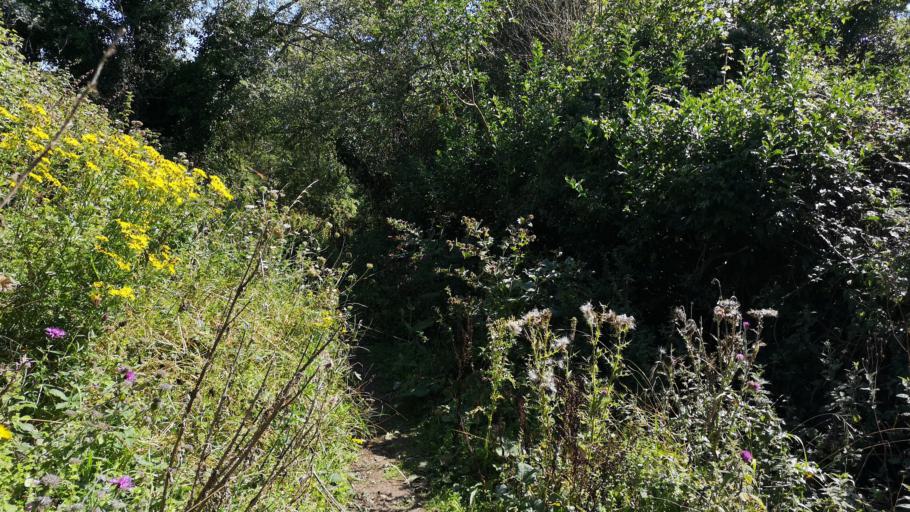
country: GB
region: England
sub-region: Isle of Wight
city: Brading
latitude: 50.6776
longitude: -1.1570
